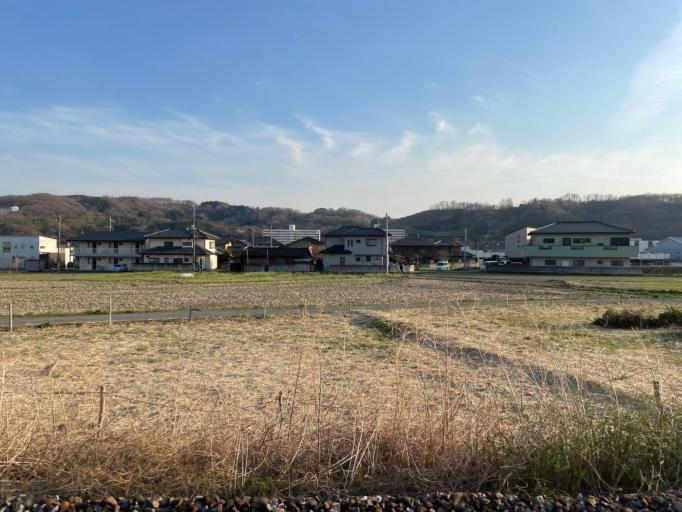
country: JP
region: Gunma
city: Annaka
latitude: 36.3378
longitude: 138.9446
